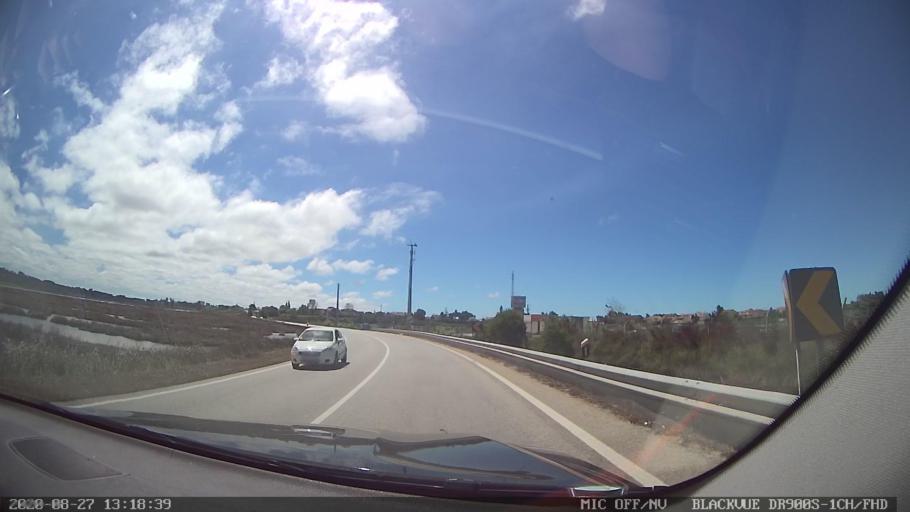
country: PT
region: Aveiro
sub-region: Vagos
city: Vagos
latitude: 40.5726
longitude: -8.6822
